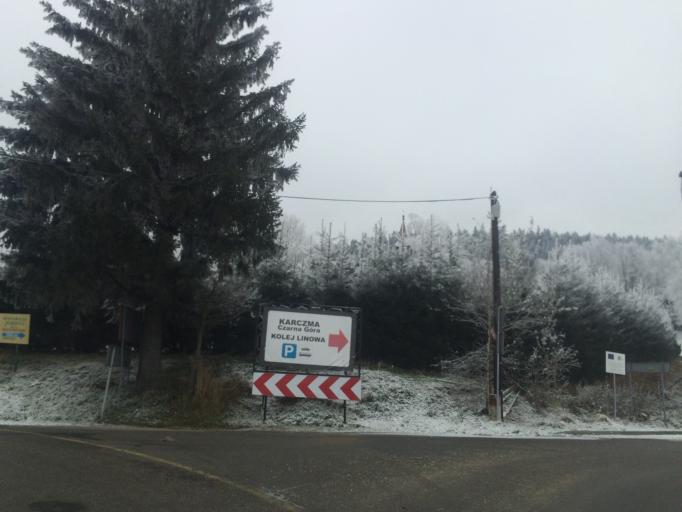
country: PL
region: Lower Silesian Voivodeship
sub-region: Powiat klodzki
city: Stronie Slaskie
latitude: 50.2608
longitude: 16.8230
